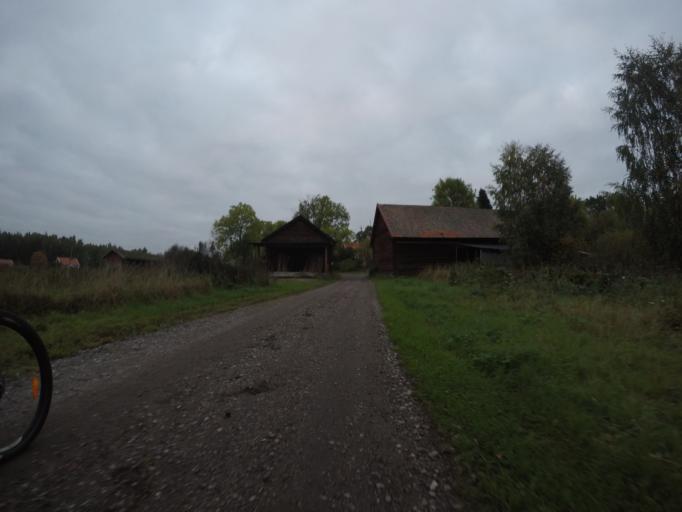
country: SE
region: Vaestmanland
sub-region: Kungsors Kommun
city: Kungsoer
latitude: 59.4022
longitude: 16.1175
